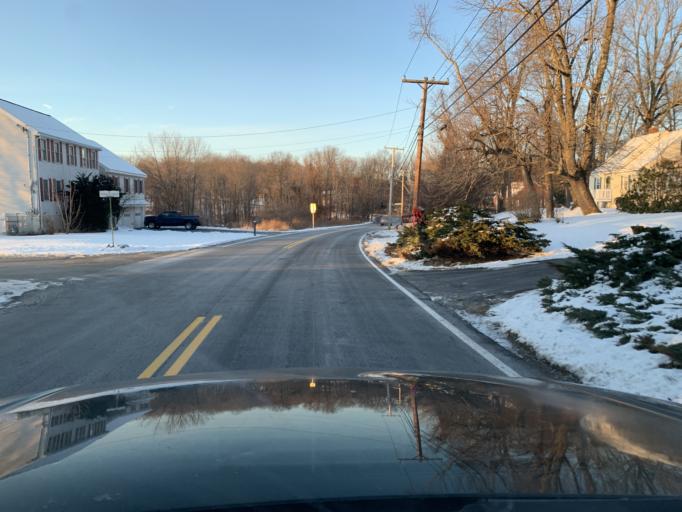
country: US
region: Massachusetts
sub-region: Essex County
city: Haverhill
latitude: 42.7904
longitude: -71.1147
